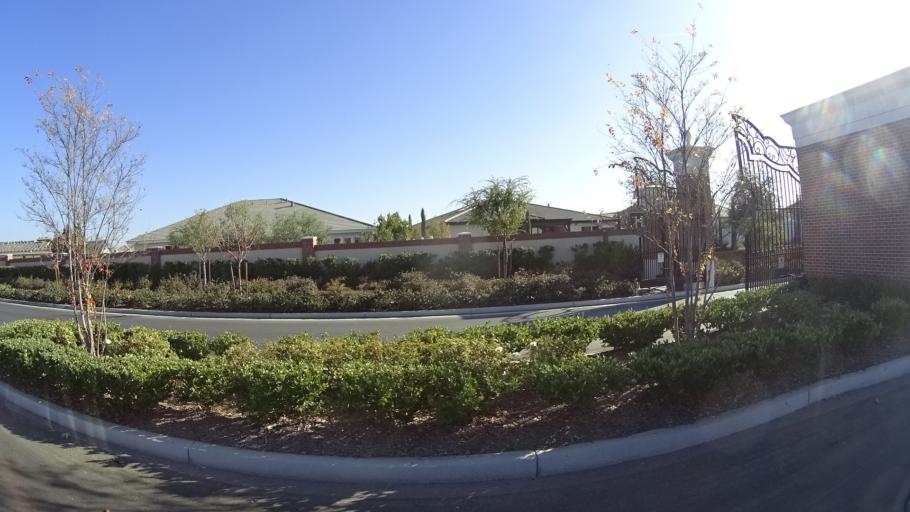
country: US
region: California
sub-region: Kern County
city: Rosedale
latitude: 35.3378
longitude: -119.1520
